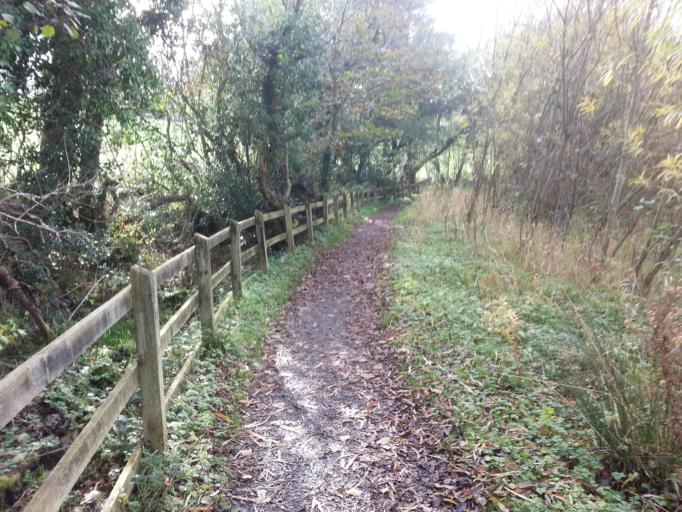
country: IE
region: Ulster
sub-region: County Monaghan
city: Clones
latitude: 54.2274
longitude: -7.2792
